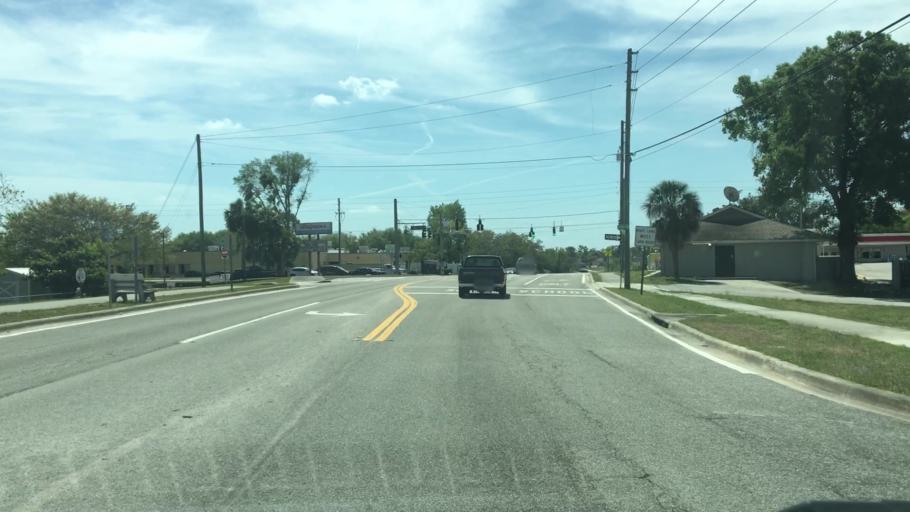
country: US
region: Florida
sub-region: Volusia County
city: Deltona
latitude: 28.9186
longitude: -81.2216
